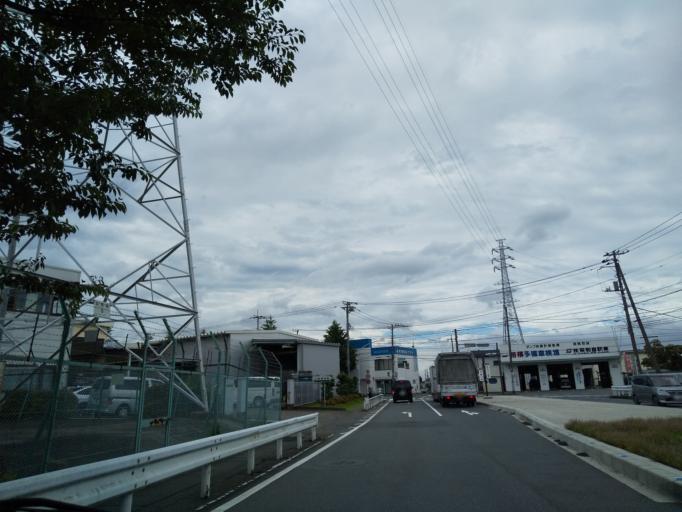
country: JP
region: Kanagawa
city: Zama
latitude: 35.5084
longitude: 139.3463
